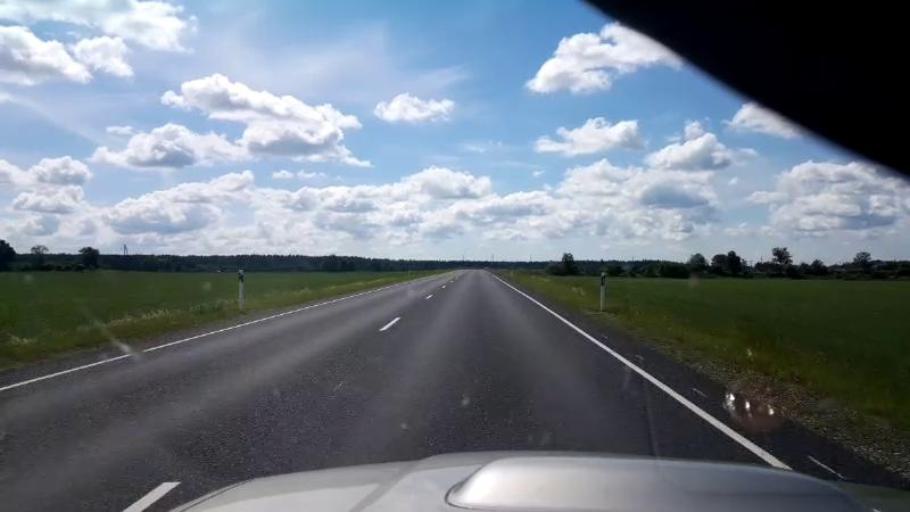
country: EE
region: Jaervamaa
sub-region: Jaerva-Jaani vald
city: Jarva-Jaani
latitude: 59.1464
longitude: 25.7706
